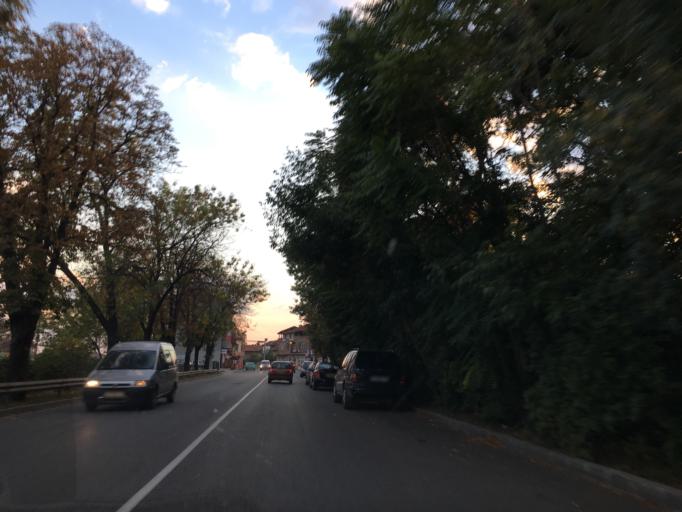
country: BG
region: Sofia-Capital
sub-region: Stolichna Obshtina
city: Sofia
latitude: 42.8016
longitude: 23.3421
